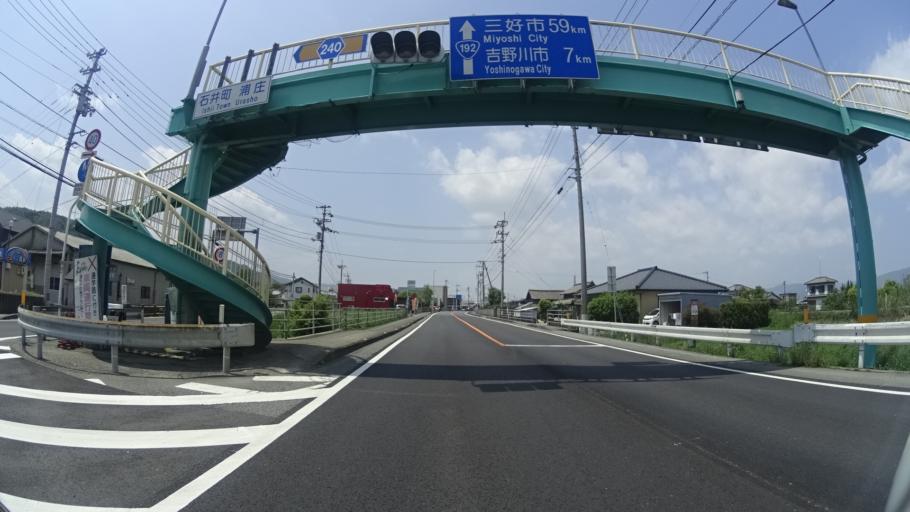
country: JP
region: Tokushima
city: Ishii
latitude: 34.0673
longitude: 134.4198
